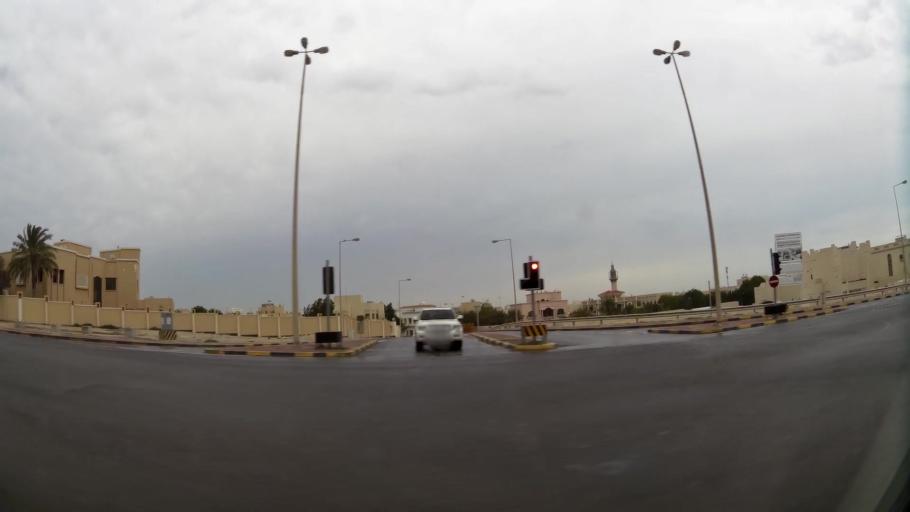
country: BH
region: Central Governorate
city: Madinat Hamad
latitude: 26.1412
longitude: 50.5171
